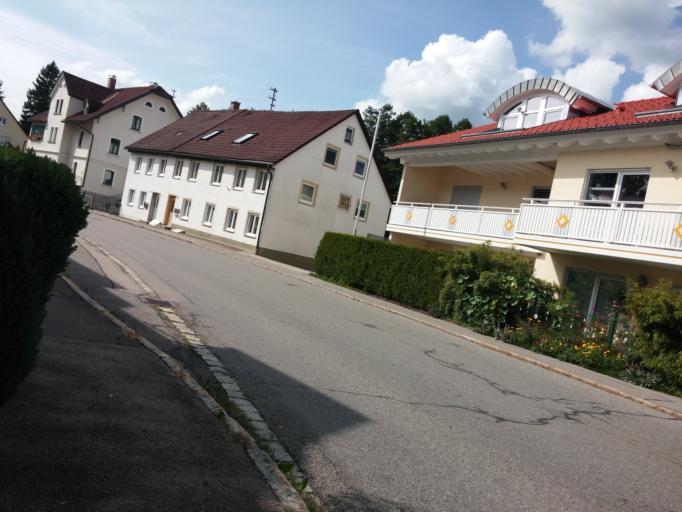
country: DE
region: Baden-Wuerttemberg
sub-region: Tuebingen Region
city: Isny im Allgau
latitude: 47.6937
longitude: 10.0481
